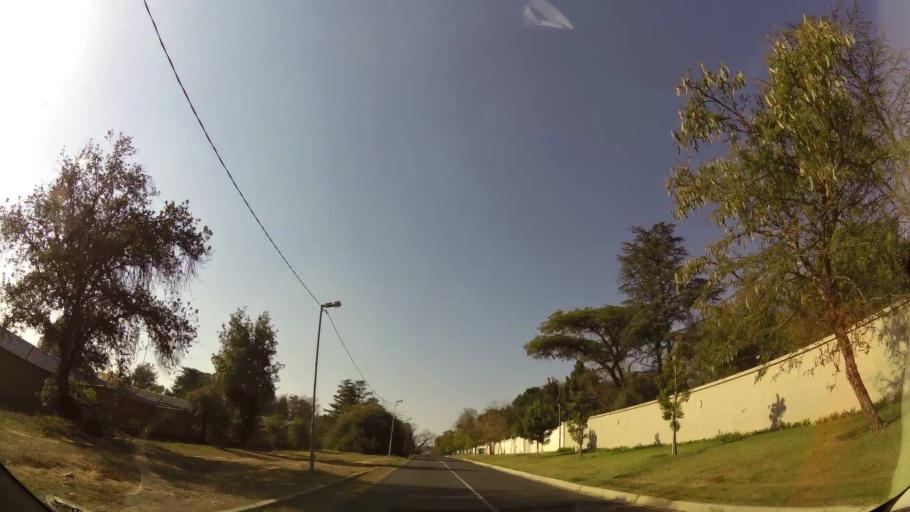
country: ZA
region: Gauteng
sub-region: City of Johannesburg Metropolitan Municipality
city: Diepsloot
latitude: -26.0647
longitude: 28.0101
